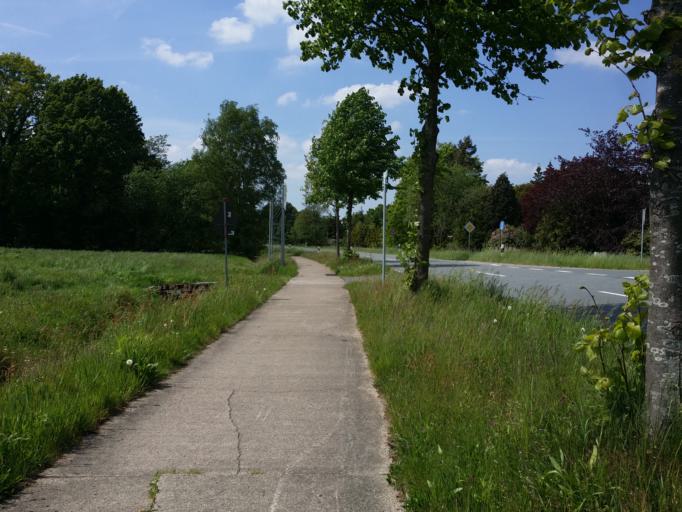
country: DE
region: Lower Saxony
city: Axstedt
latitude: 53.2994
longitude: 8.7611
